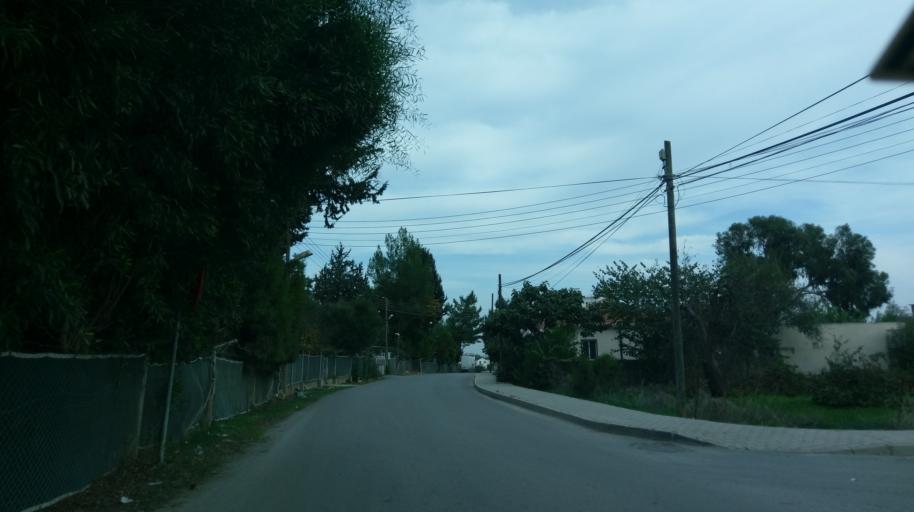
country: CY
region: Keryneia
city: Kyrenia
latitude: 35.2661
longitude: 33.3286
